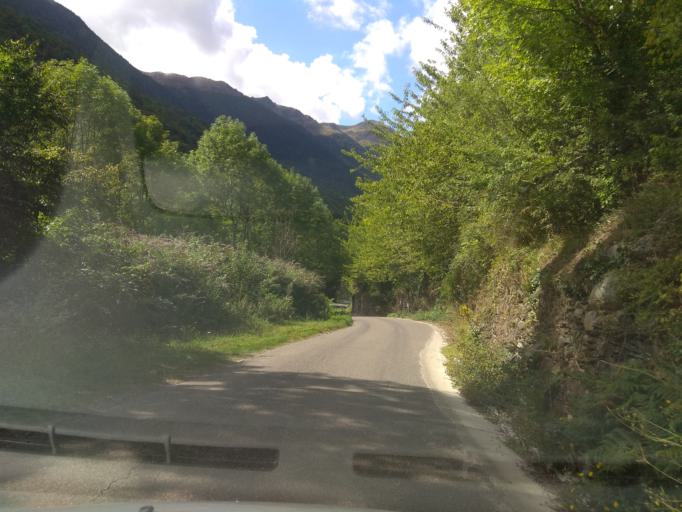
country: ES
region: Catalonia
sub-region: Provincia de Lleida
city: Vielha
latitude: 42.7319
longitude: 0.7246
